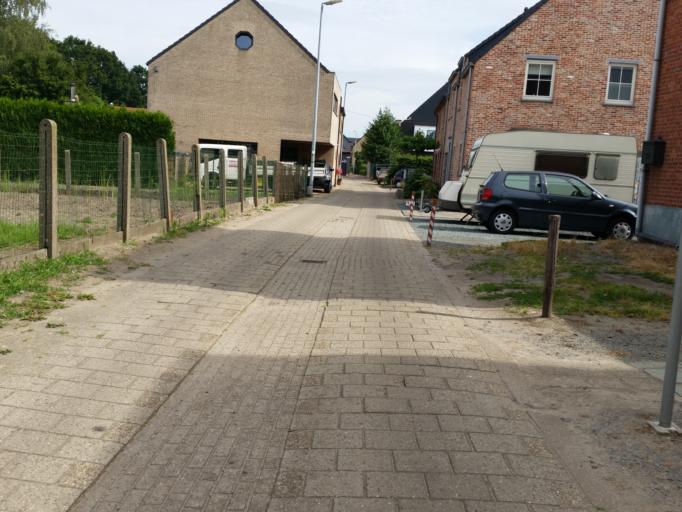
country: BE
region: Flanders
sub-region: Provincie Antwerpen
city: Puurs
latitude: 51.1019
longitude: 4.3019
